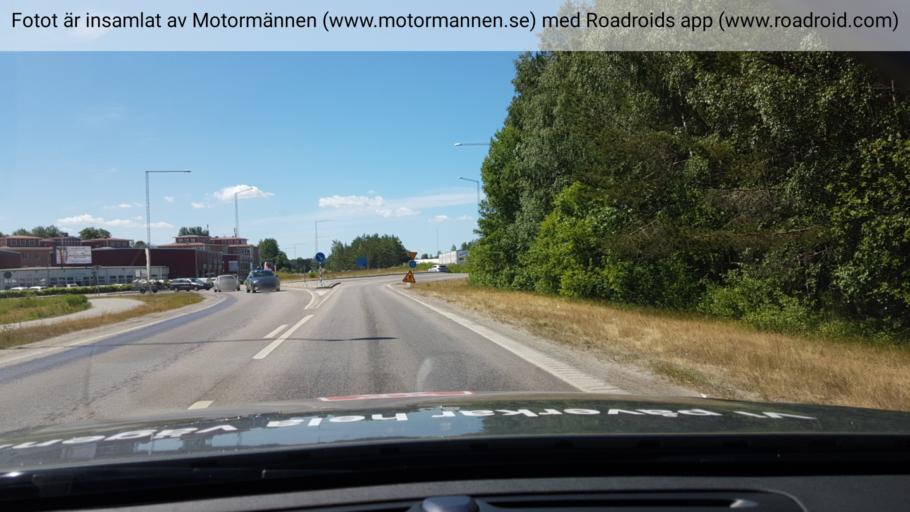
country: SE
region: Stockholm
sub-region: Haninge Kommun
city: Haninge
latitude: 59.1919
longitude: 18.1787
